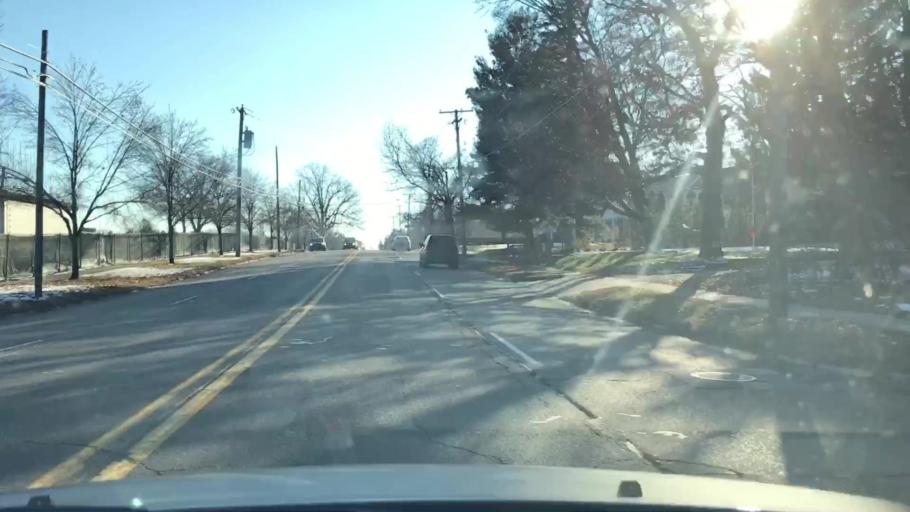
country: US
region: Michigan
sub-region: Oakland County
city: Royal Oak
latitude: 42.5087
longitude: -83.1421
